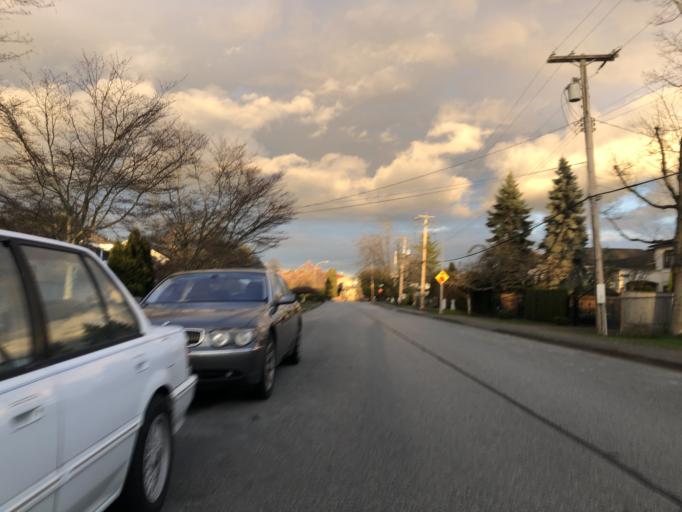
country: CA
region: British Columbia
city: Richmond
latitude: 49.1500
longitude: -123.1215
